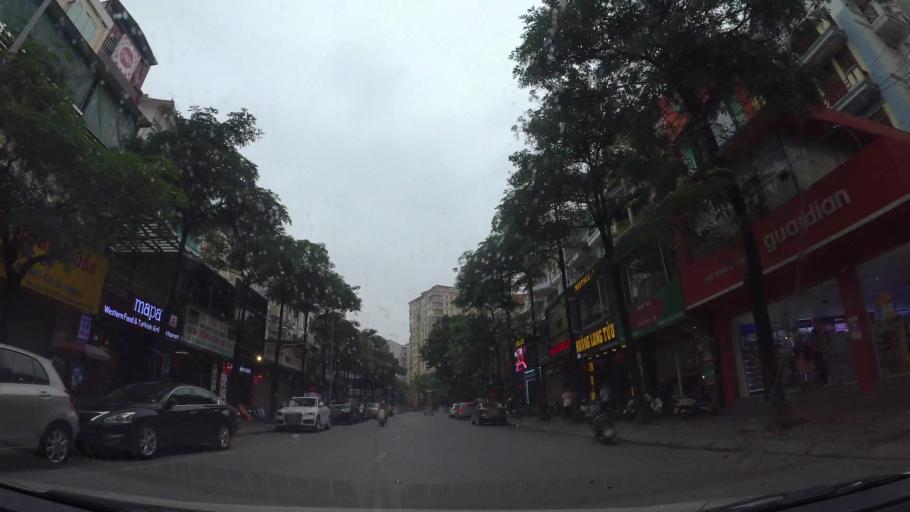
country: VN
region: Ha Noi
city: Cau Giay
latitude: 21.0163
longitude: 105.8000
